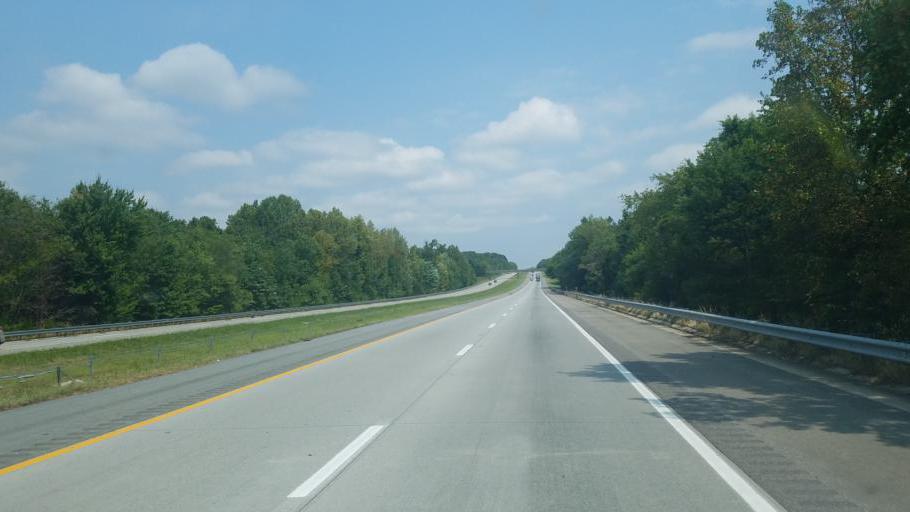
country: US
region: North Carolina
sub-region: Yadkin County
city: Jonesville
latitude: 36.1514
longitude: -80.8078
